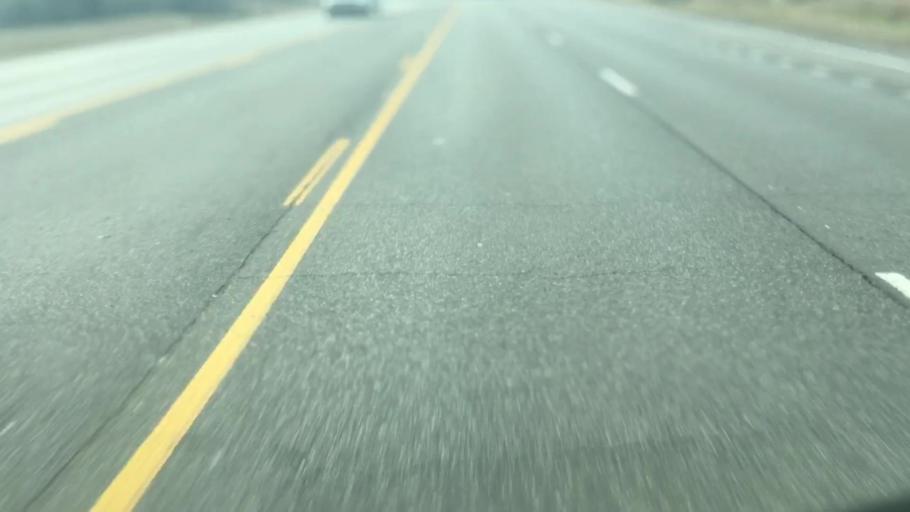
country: US
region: Alabama
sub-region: Walker County
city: Jasper
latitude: 33.8210
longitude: -87.2339
